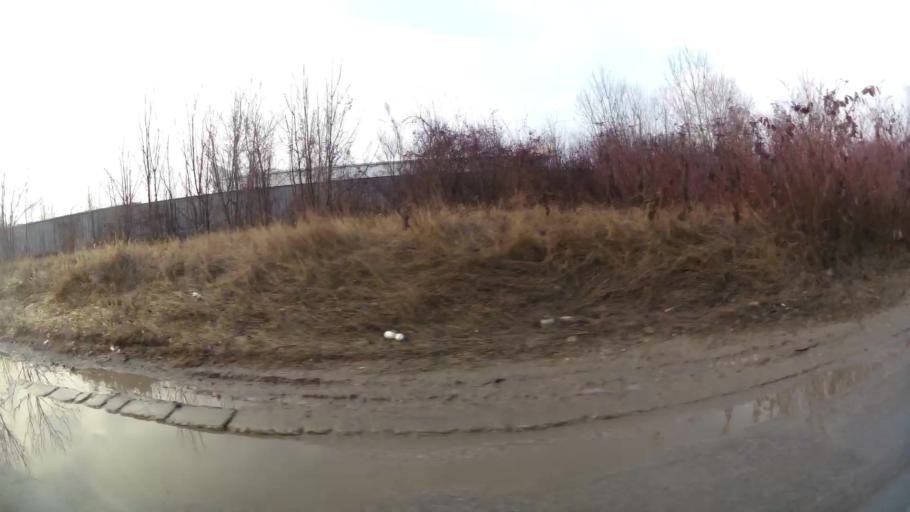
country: BG
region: Sofia-Capital
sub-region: Stolichna Obshtina
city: Sofia
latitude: 42.7410
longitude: 23.3299
